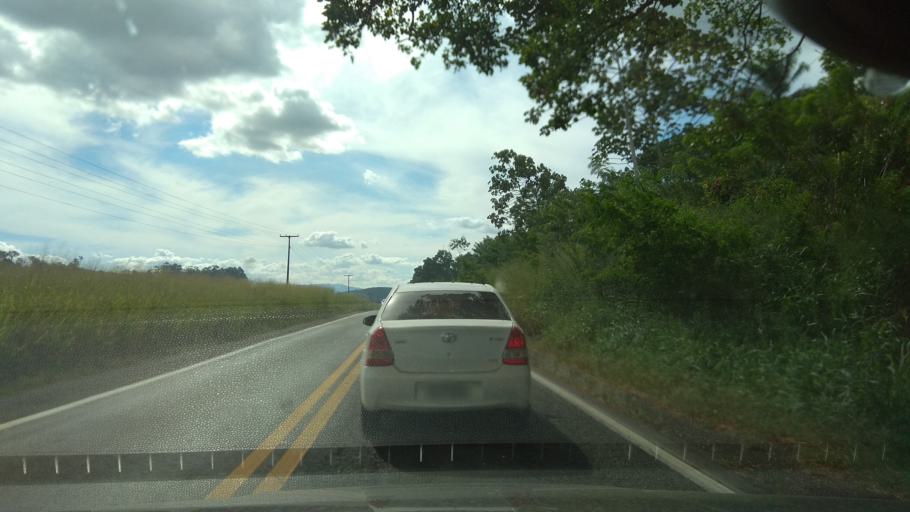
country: BR
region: Bahia
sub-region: Ipiau
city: Ipiau
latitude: -14.0790
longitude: -39.7820
